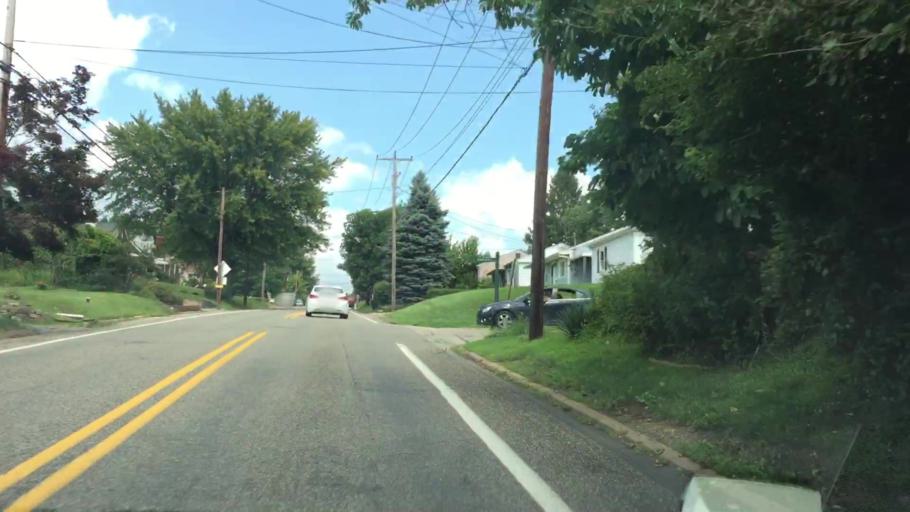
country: US
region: Pennsylvania
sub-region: Allegheny County
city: Cheswick
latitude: 40.5467
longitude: -79.8044
